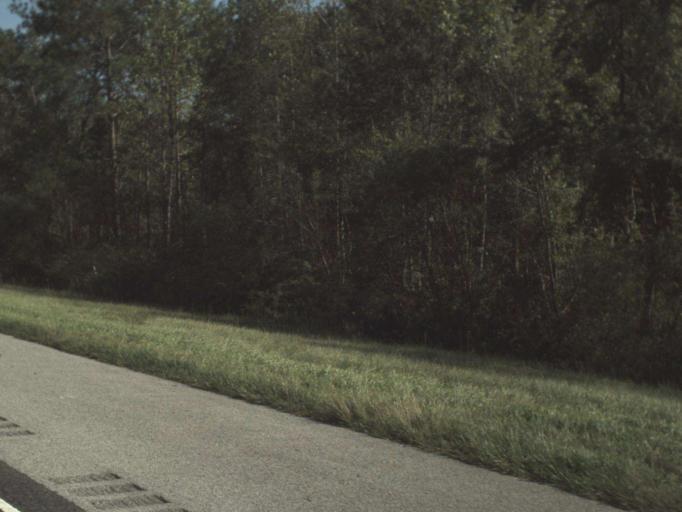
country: US
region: Florida
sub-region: Washington County
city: Chipley
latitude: 30.7511
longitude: -85.5753
